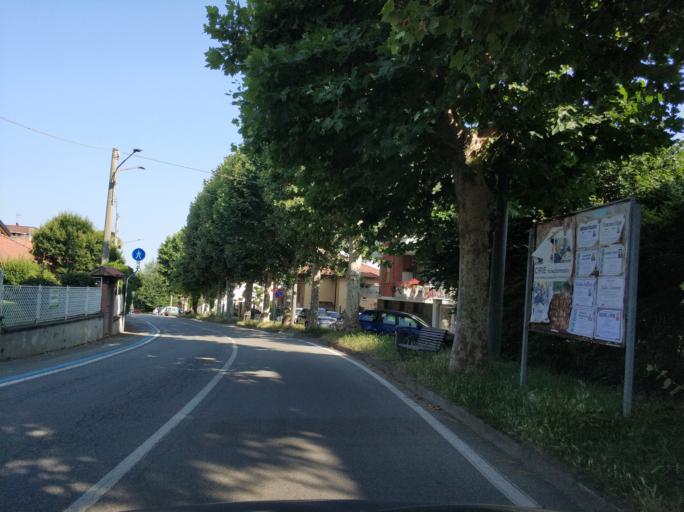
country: IT
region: Piedmont
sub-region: Provincia di Torino
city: Fiano
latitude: 45.2173
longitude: 7.5187
